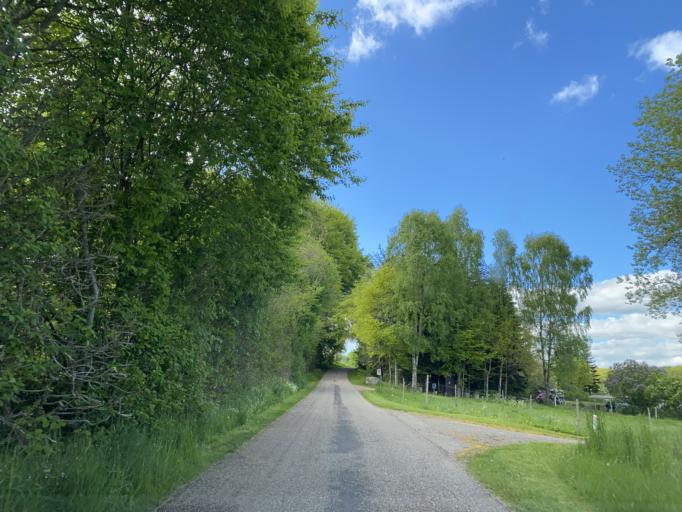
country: DK
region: Central Jutland
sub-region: Skanderborg Kommune
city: Galten
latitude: 56.1656
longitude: 9.8525
